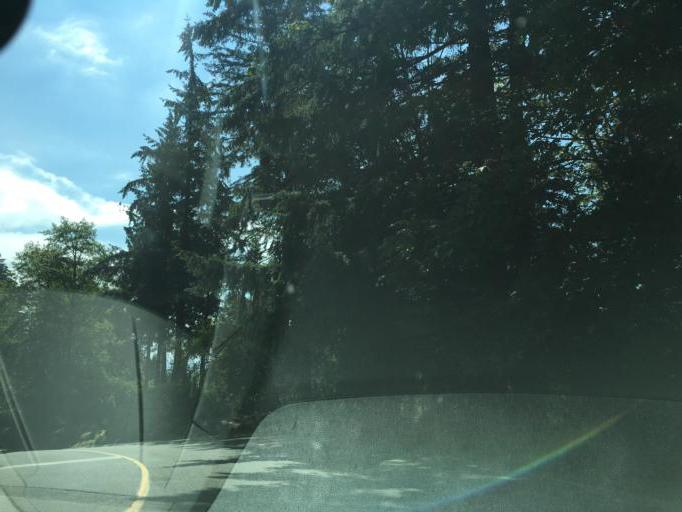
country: CA
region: British Columbia
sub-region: Greater Vancouver Regional District
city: Bowen Island
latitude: 49.3418
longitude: -123.2602
